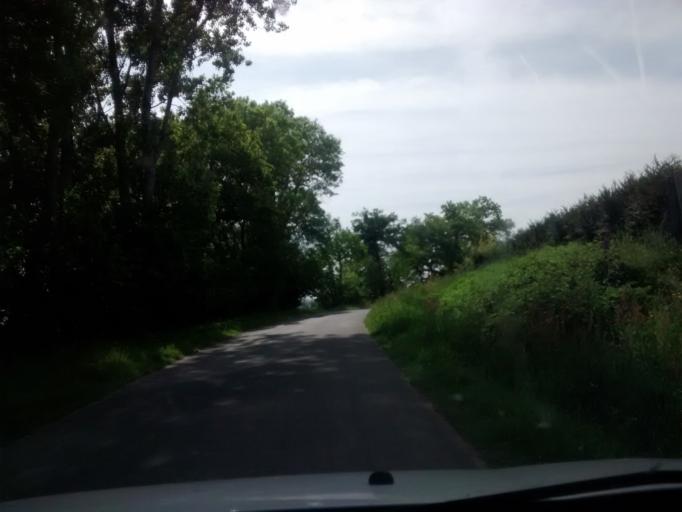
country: FR
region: Lower Normandy
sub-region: Departement de la Manche
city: Pontorson
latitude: 48.5119
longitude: -1.5119
